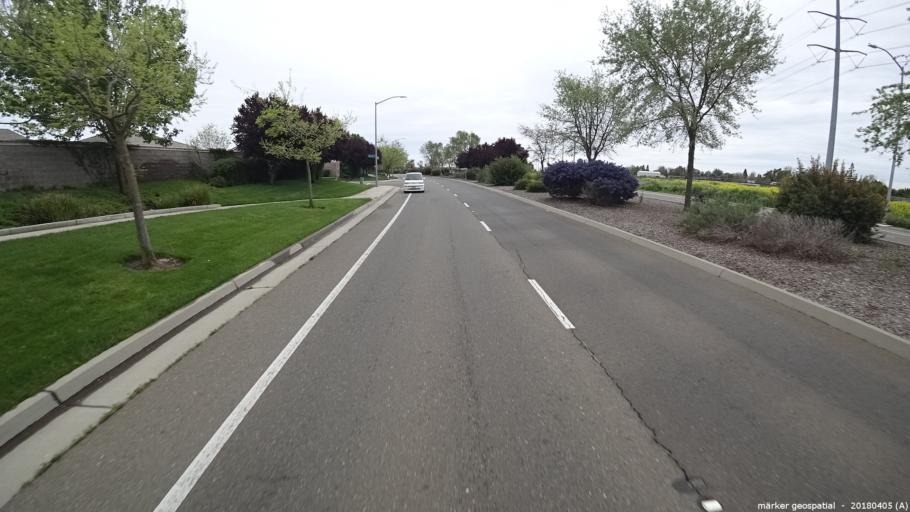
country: US
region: California
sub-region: Sacramento County
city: Laguna
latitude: 38.3846
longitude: -121.4510
